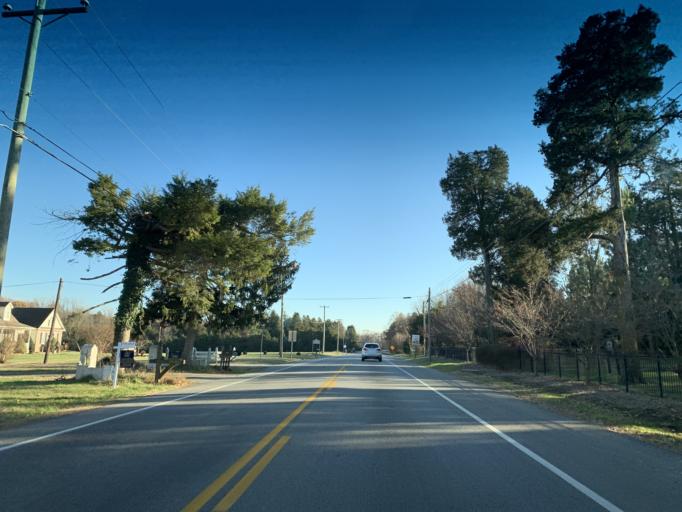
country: US
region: Delaware
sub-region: New Castle County
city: Middletown
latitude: 39.3589
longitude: -75.8788
